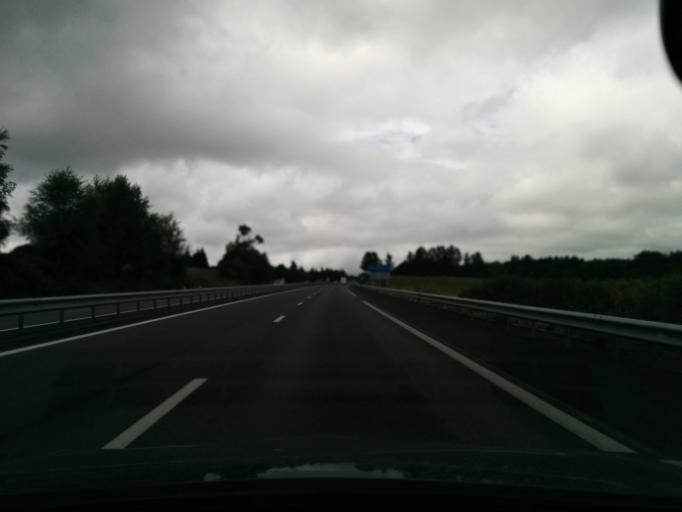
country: FR
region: Limousin
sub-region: Departement de la Correze
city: Vigeois
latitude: 45.3536
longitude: 1.5694
